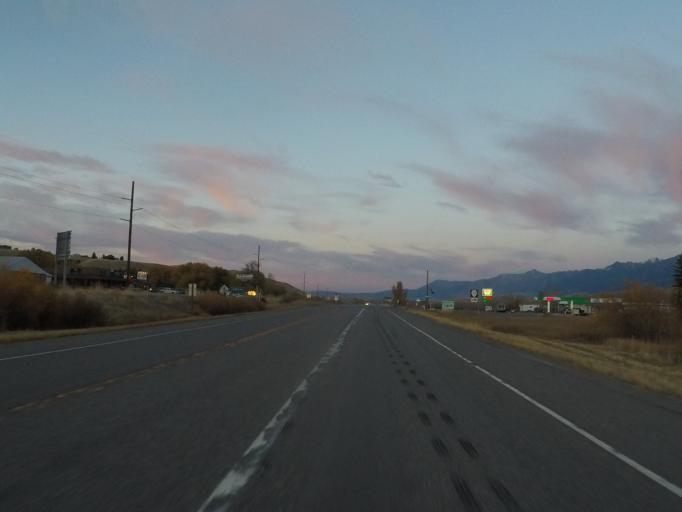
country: US
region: Montana
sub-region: Park County
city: Livingston
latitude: 45.3678
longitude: -110.7345
